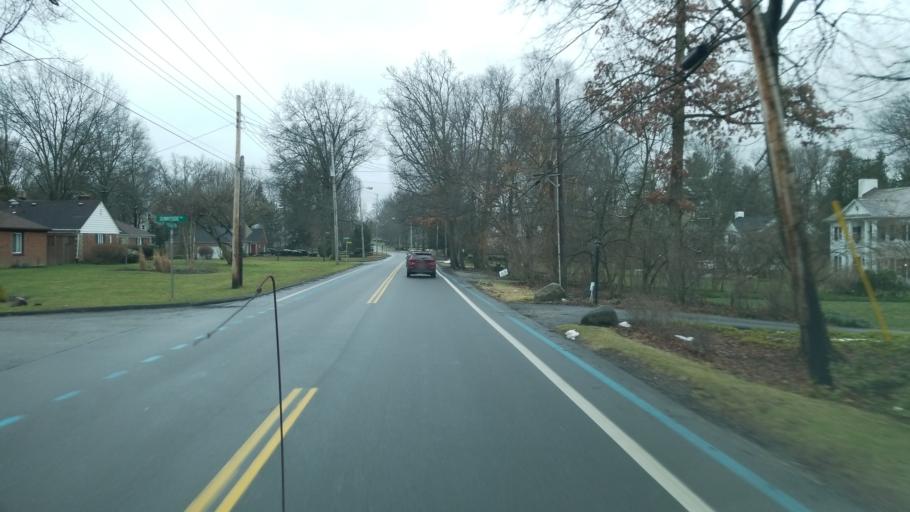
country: US
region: Ohio
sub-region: Summit County
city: Akron
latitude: 41.1124
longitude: -81.5486
